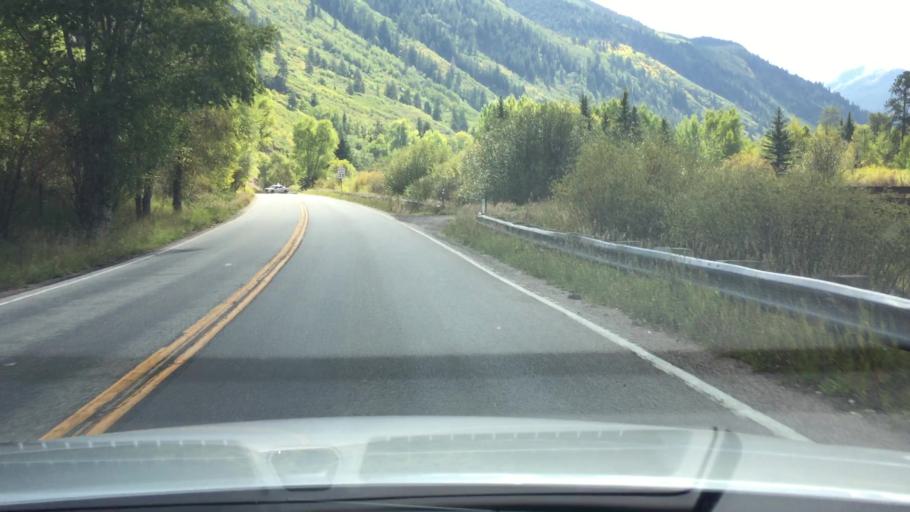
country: US
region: Colorado
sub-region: Pitkin County
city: Aspen
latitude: 39.1784
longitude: -106.8000
